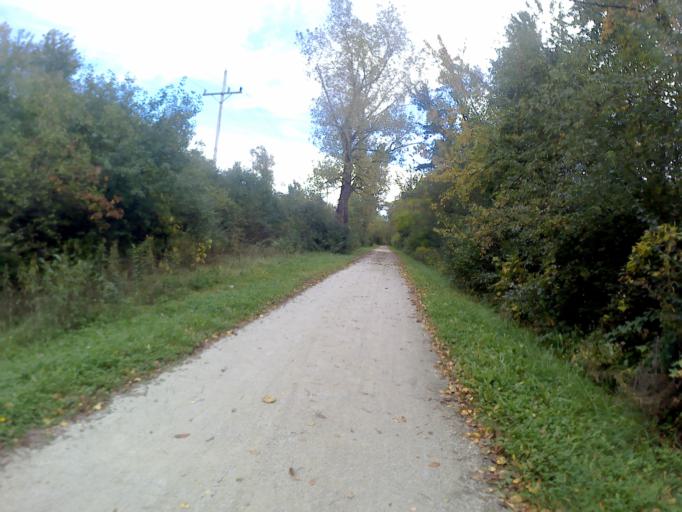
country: US
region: Illinois
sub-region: DuPage County
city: Wayne
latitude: 41.9611
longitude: -88.2525
